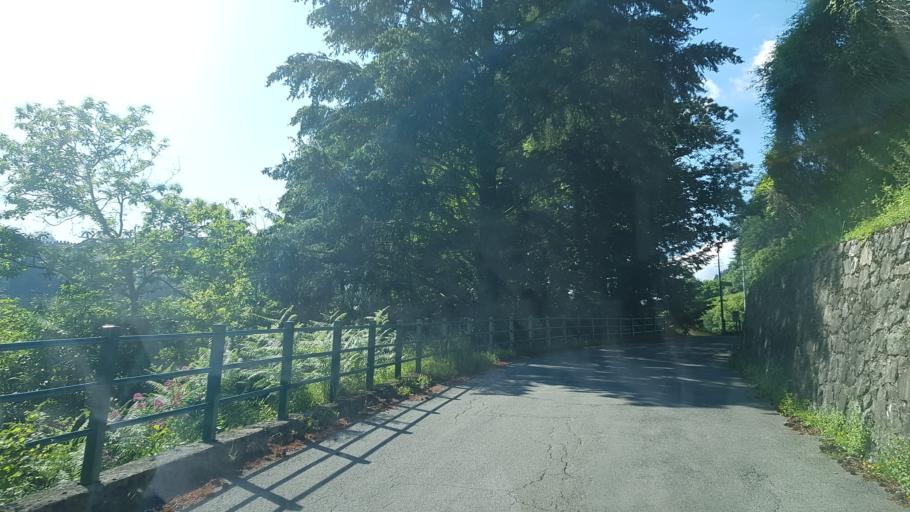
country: IT
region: Tuscany
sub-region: Provincia di Lucca
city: San Romano
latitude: 44.1783
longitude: 10.3386
